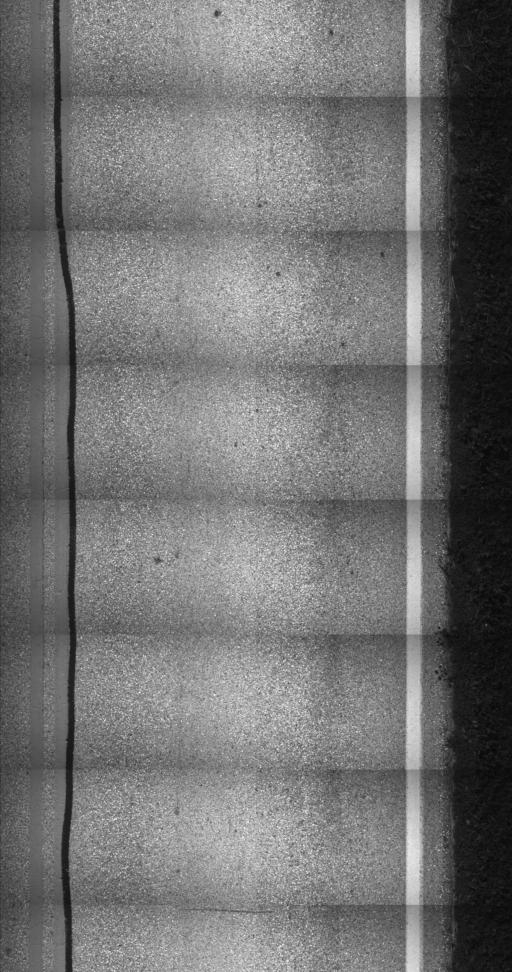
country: US
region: New York
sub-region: Washington County
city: Granville
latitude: 43.4232
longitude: -73.1183
